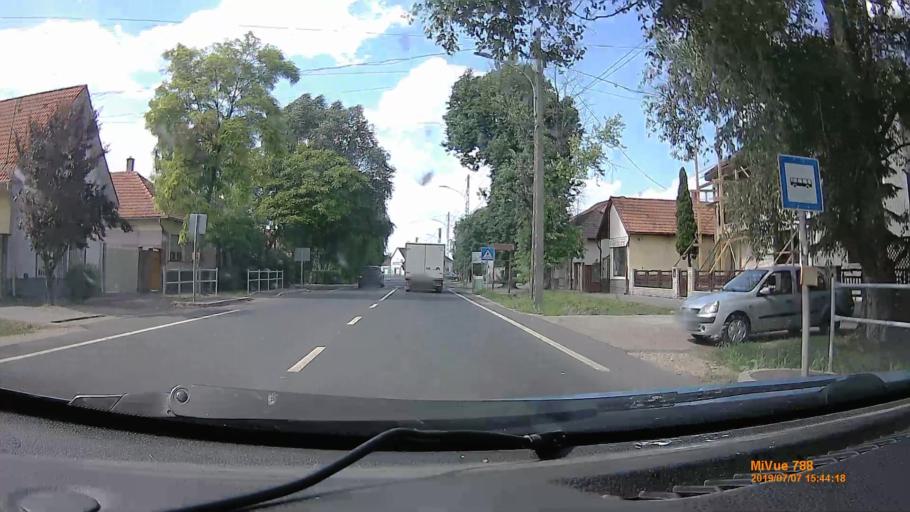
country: HU
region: Jasz-Nagykun-Szolnok
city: Jaszbereny
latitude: 47.5080
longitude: 19.9097
